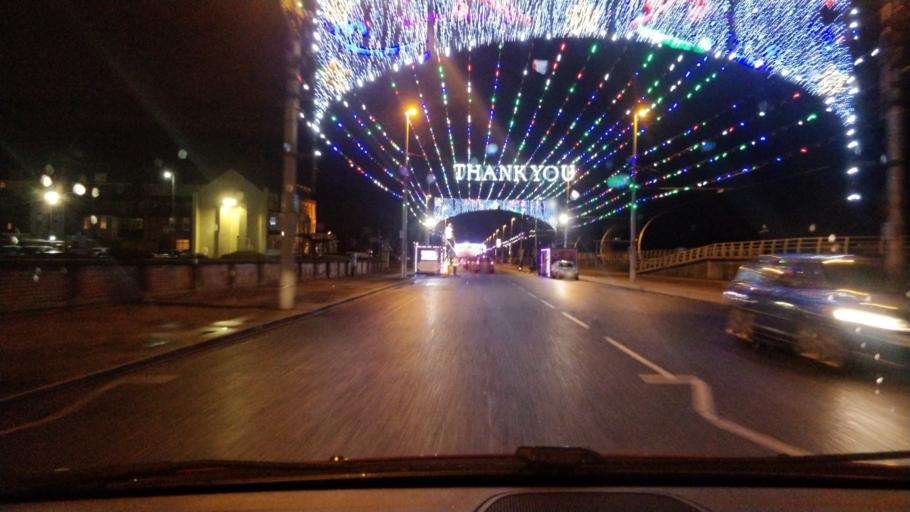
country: GB
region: England
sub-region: Blackpool
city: Blackpool
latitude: 53.7853
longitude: -3.0581
